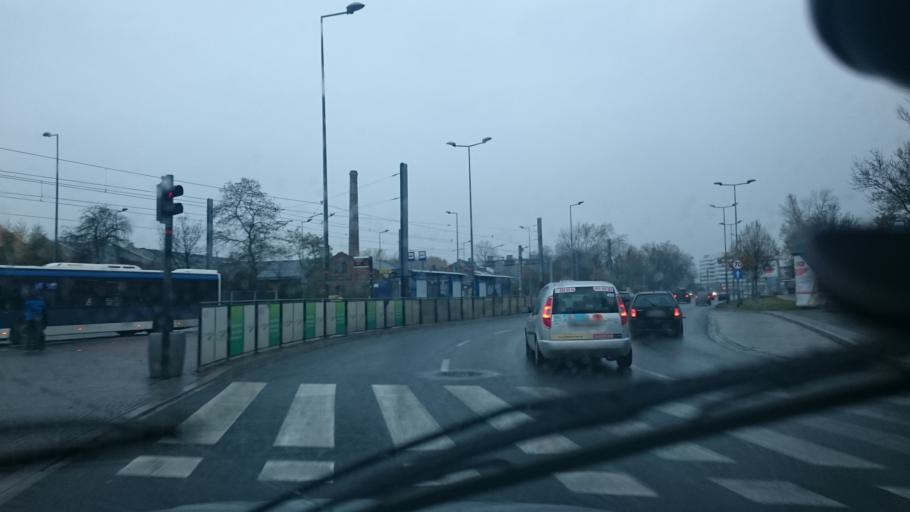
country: PL
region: Lesser Poland Voivodeship
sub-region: Krakow
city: Krakow
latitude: 50.0580
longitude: 19.9595
